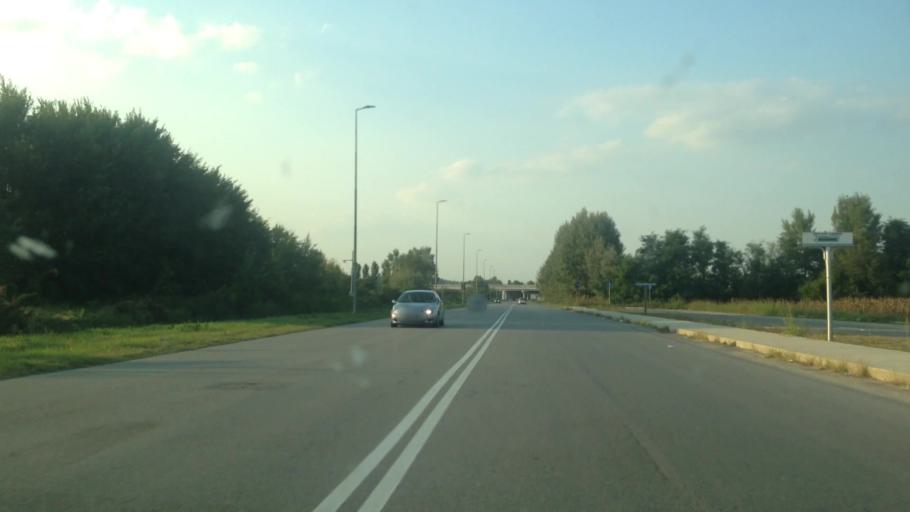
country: IT
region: Piedmont
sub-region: Provincia di Asti
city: Asti
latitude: 44.9073
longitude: 8.2311
